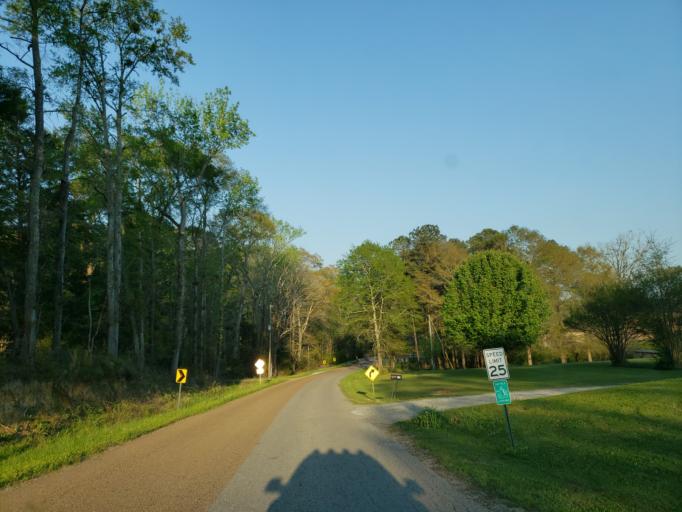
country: US
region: Mississippi
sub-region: Lauderdale County
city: Marion
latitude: 32.4034
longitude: -88.5933
